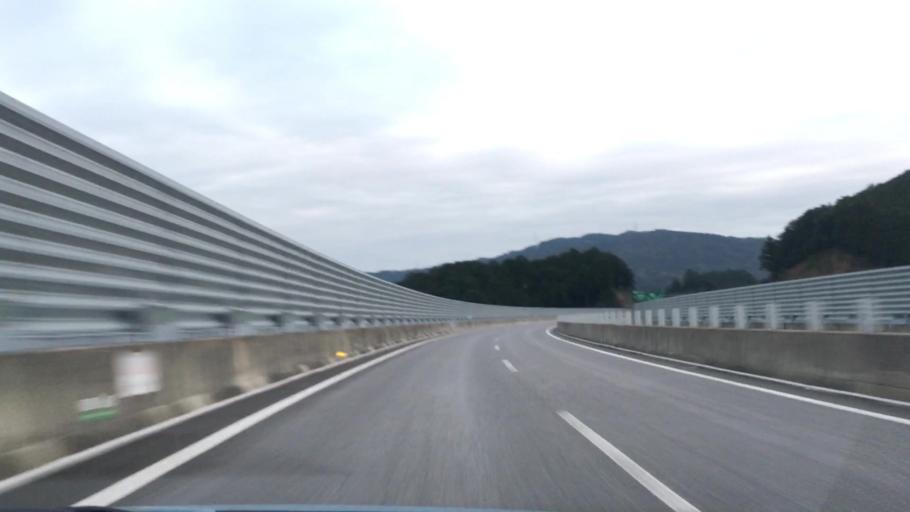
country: JP
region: Aichi
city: Shinshiro
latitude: 34.8921
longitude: 137.6565
